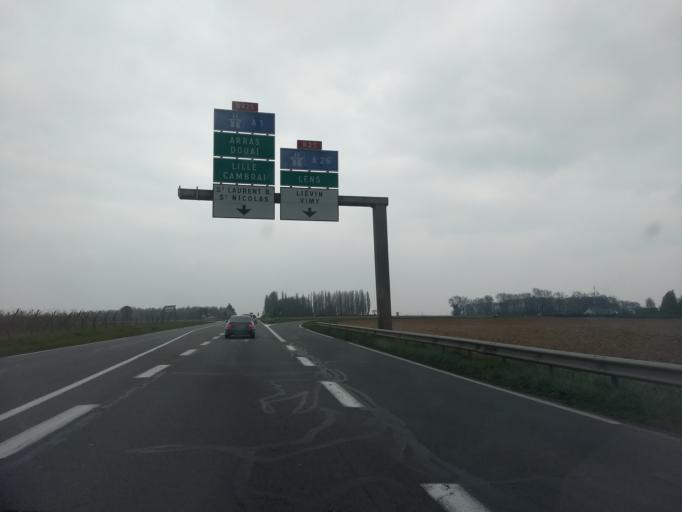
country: FR
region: Nord-Pas-de-Calais
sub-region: Departement du Pas-de-Calais
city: Sainte-Catherine
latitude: 50.3222
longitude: 2.7635
